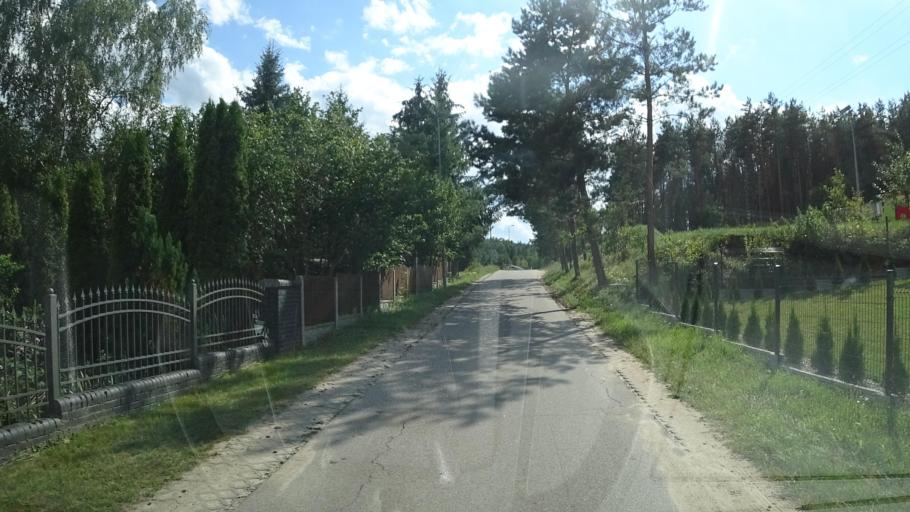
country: PL
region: Podlasie
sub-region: Powiat lomzynski
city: Piatnica
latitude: 53.1427
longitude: 22.1271
